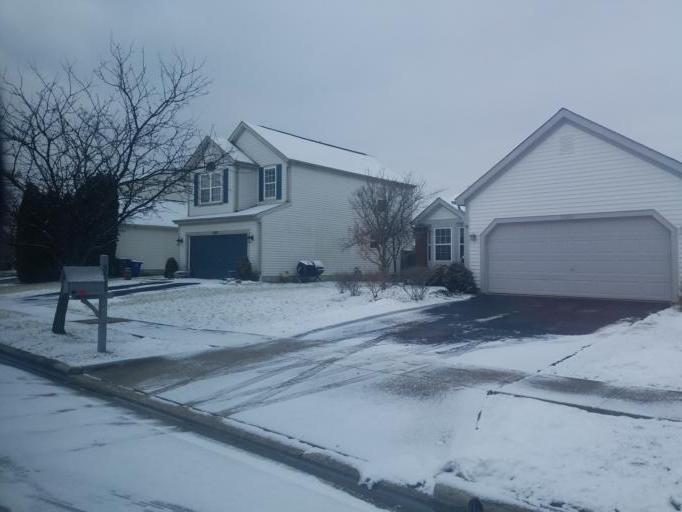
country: US
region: Ohio
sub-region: Franklin County
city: Reynoldsburg
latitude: 39.9962
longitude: -82.7782
